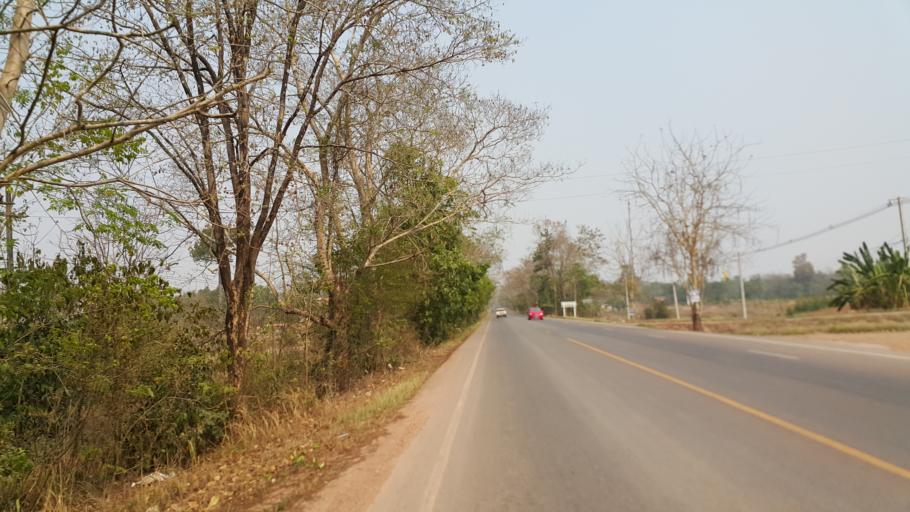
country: TH
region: Nakhon Phanom
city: Ban Phaeng
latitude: 17.8388
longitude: 104.2647
